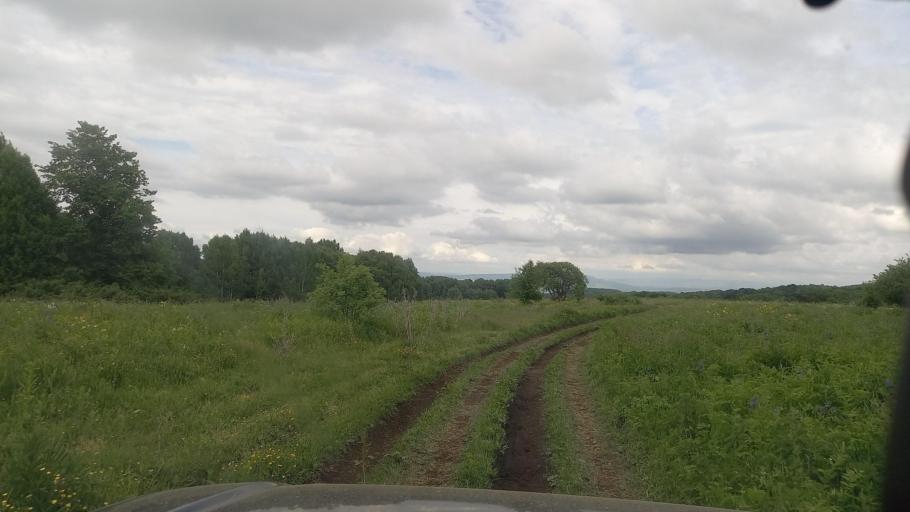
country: RU
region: Karachayevo-Cherkesiya
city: Pregradnaya
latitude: 44.0205
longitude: 41.2874
